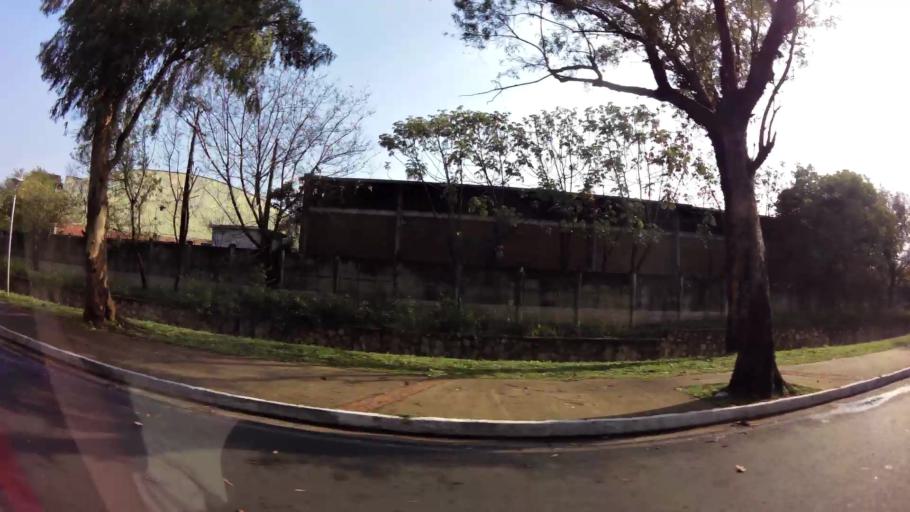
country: PY
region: Presidente Hayes
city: Nanawa
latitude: -25.2761
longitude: -57.6450
